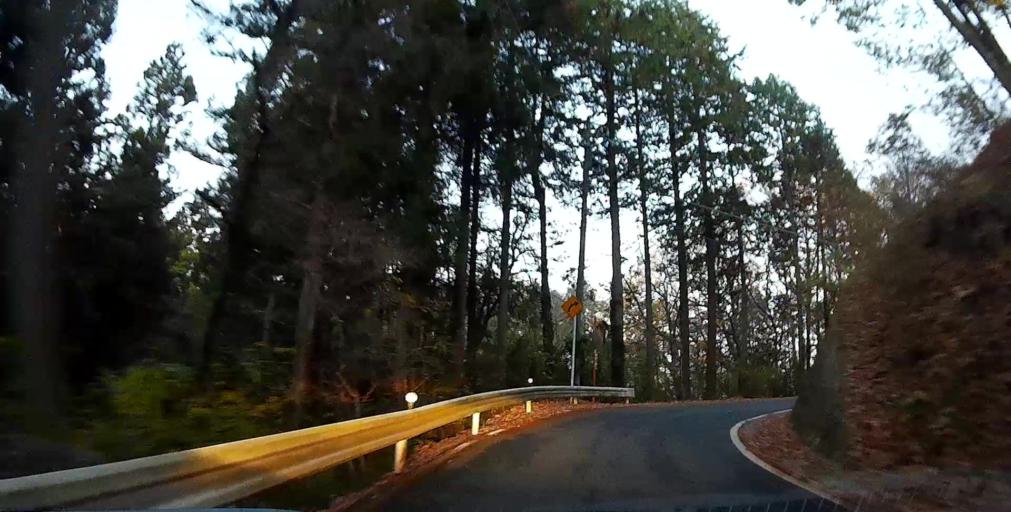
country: JP
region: Yamanashi
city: Uenohara
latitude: 35.6009
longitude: 139.1863
